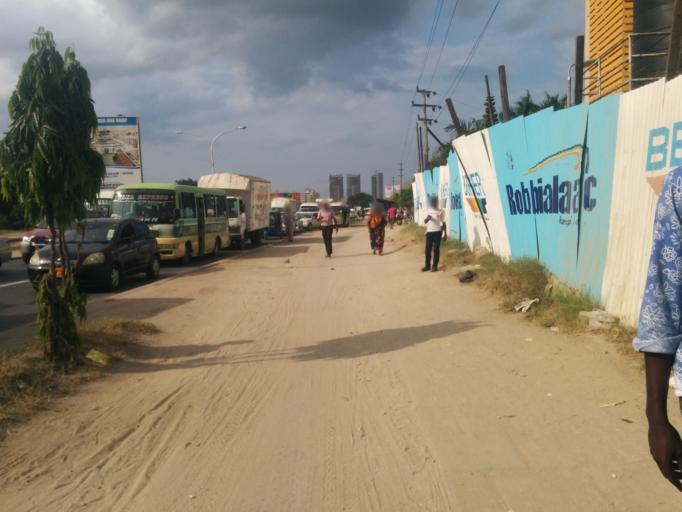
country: TZ
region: Dar es Salaam
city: Dar es Salaam
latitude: -6.8312
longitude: 39.2704
